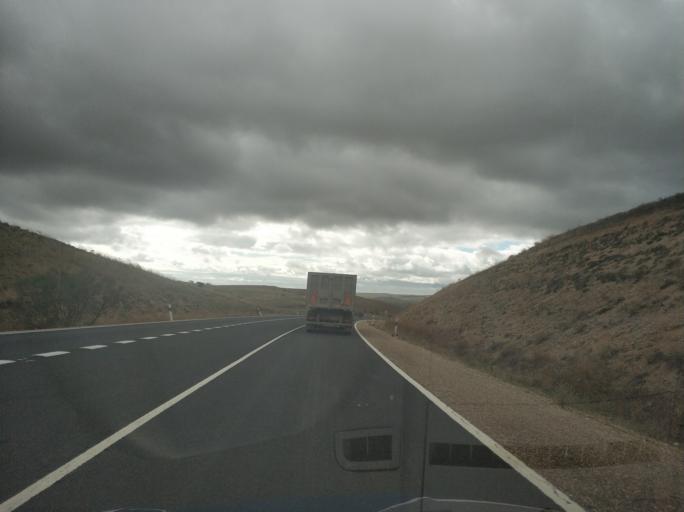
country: ES
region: Castille and Leon
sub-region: Provincia de Zamora
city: Castrillo de la Guarena
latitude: 41.2409
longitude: -5.2964
